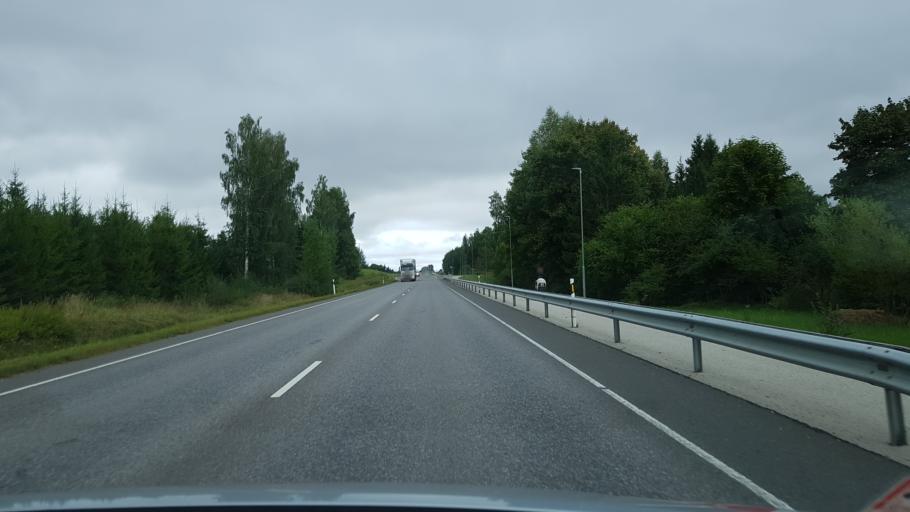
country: EE
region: Vorumaa
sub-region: Voru linn
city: Voru
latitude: 57.8736
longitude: 26.9944
